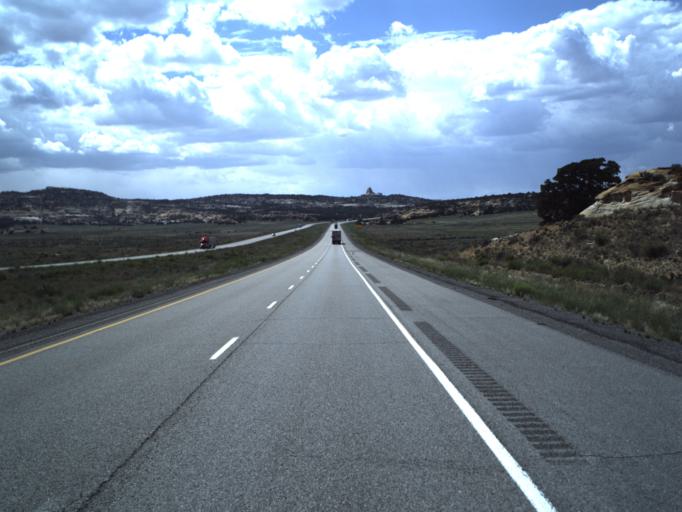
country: US
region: Utah
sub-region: Emery County
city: Castle Dale
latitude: 38.8689
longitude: -110.7769
